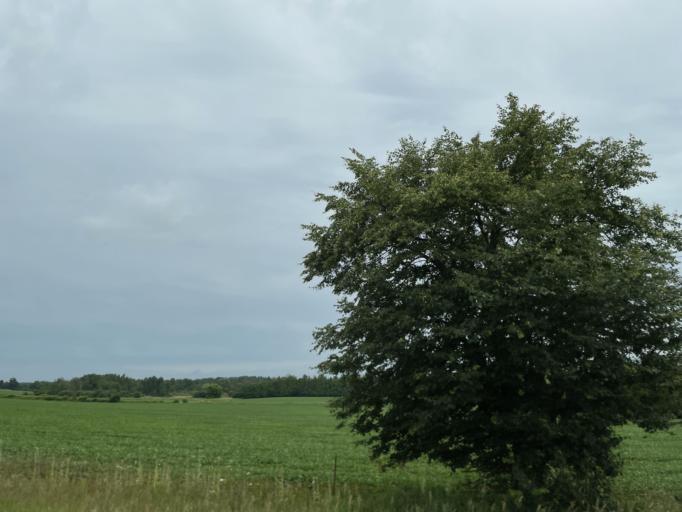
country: CA
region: Ontario
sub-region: Wellington County
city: Guelph
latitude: 43.5816
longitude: -80.3042
